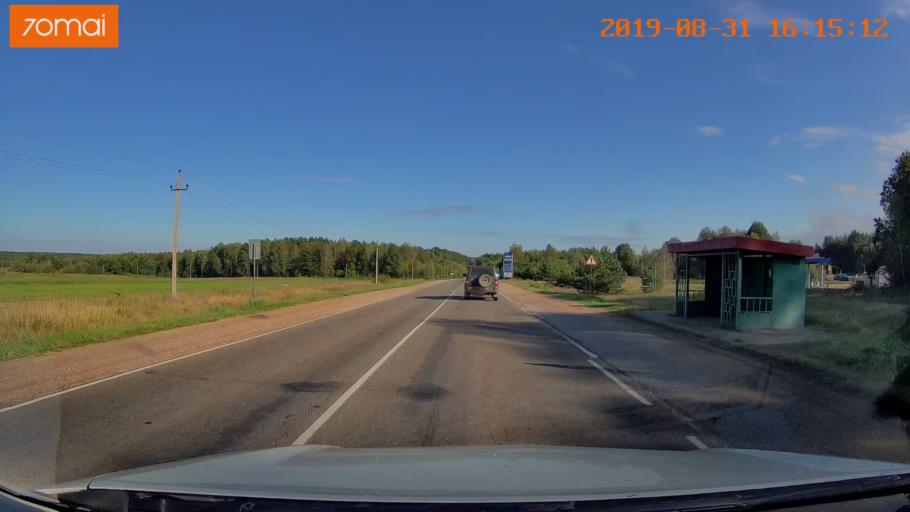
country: RU
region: Kaluga
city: Nikola-Lenivets
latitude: 54.5614
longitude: 35.4834
